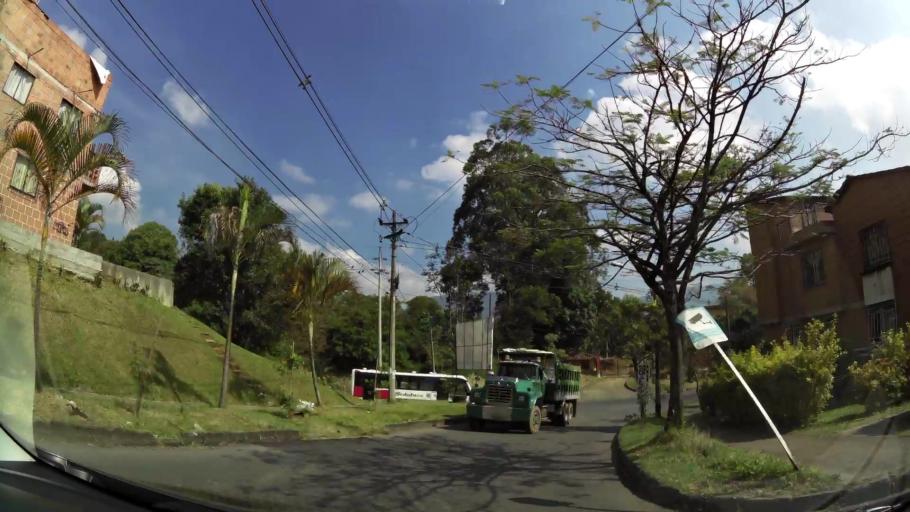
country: CO
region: Antioquia
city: La Estrella
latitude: 6.1668
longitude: -75.6443
